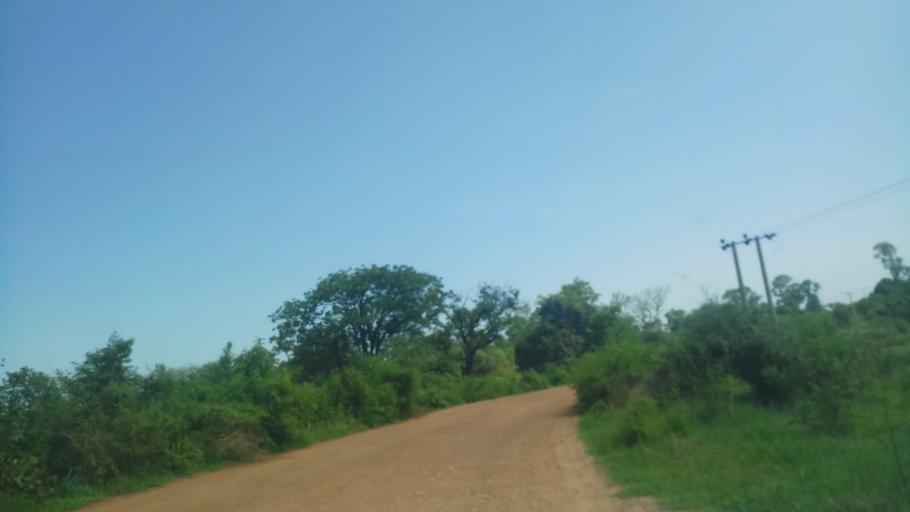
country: ET
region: Gambela
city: Gambela
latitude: 8.2188
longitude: 34.5641
